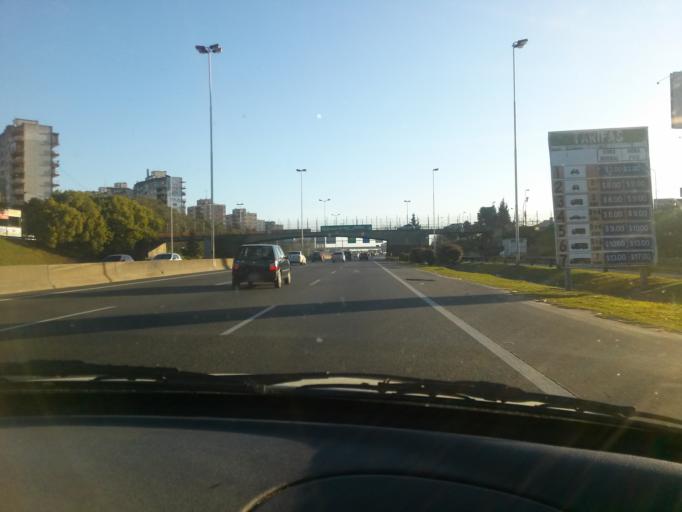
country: AR
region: Buenos Aires F.D.
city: Villa Lugano
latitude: -34.6939
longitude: -58.4912
